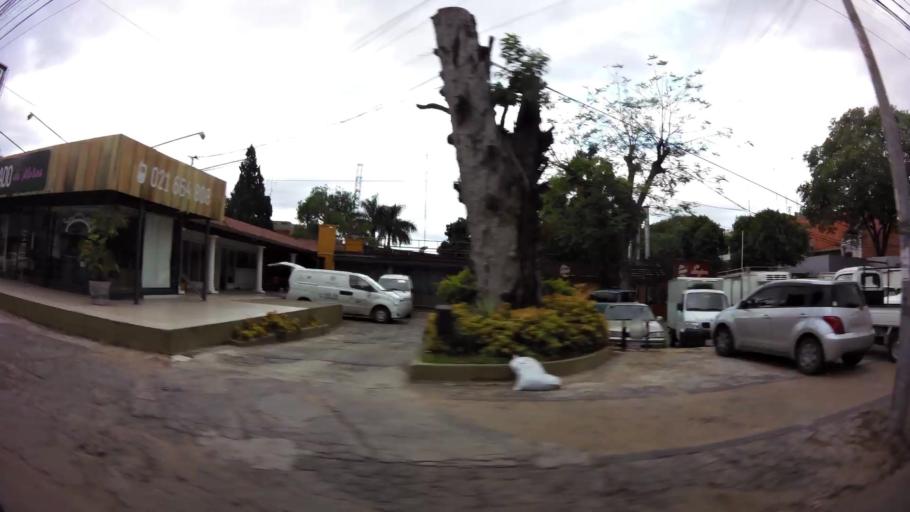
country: PY
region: Asuncion
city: Asuncion
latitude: -25.2858
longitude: -57.5747
